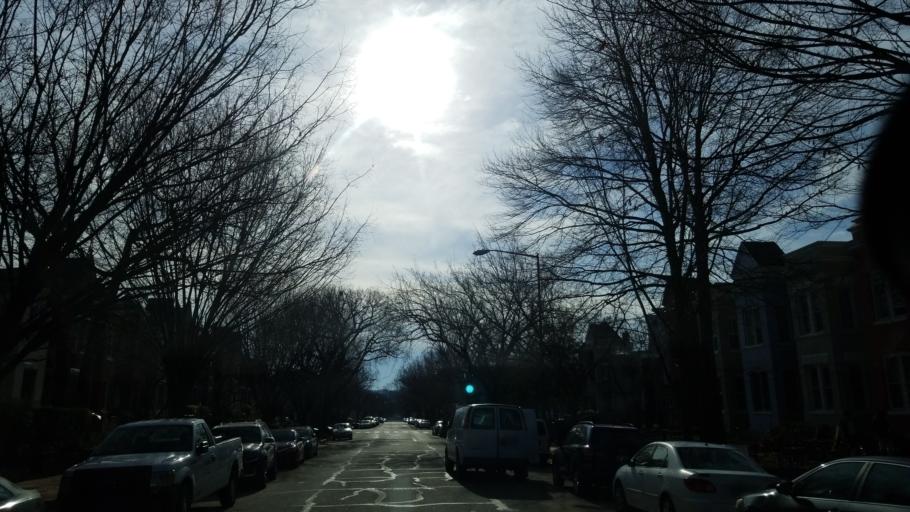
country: US
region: Washington, D.C.
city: Washington, D.C.
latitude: 38.8836
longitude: -76.9851
